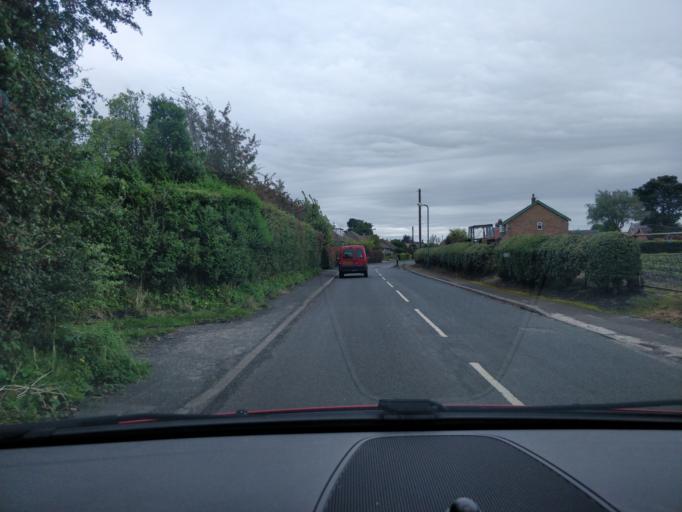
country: GB
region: England
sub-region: Lancashire
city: Ormskirk
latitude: 53.6106
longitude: -2.8416
